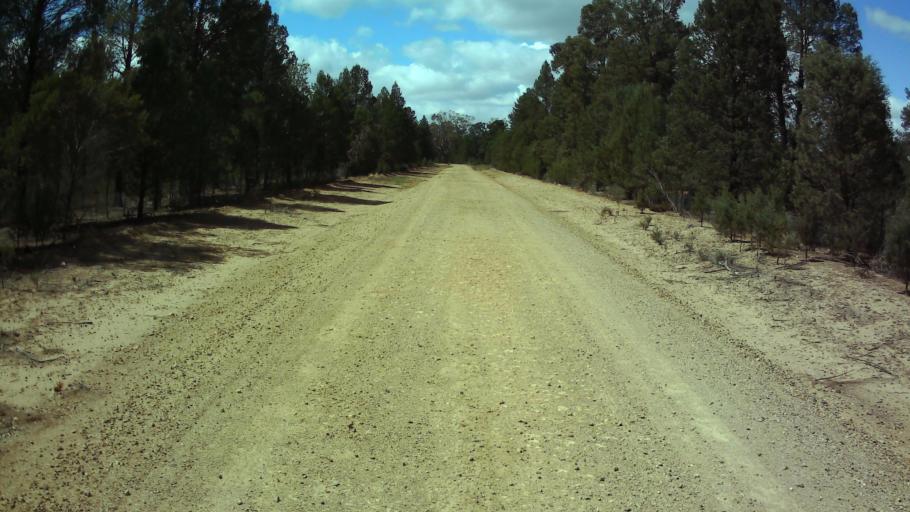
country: AU
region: New South Wales
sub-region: Weddin
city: Grenfell
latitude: -33.9147
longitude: 147.9214
